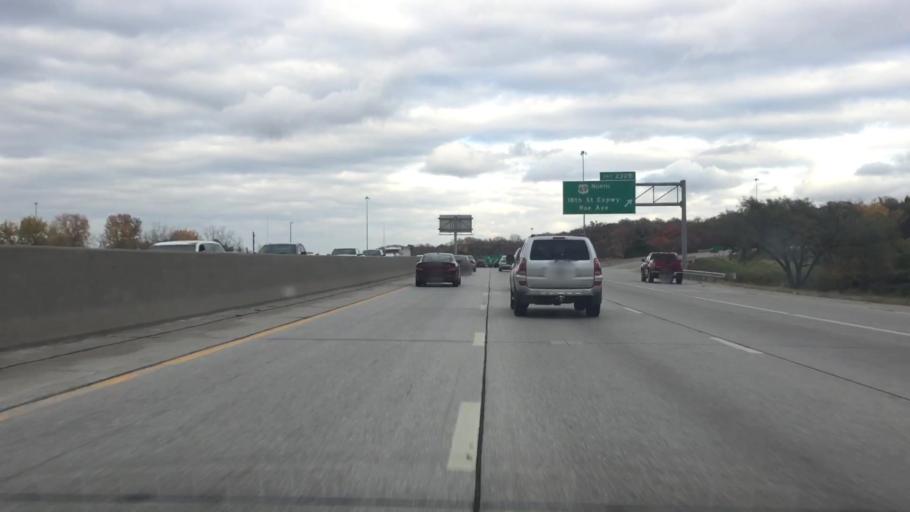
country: US
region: Kansas
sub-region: Johnson County
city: Mission
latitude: 39.0465
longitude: -94.6510
